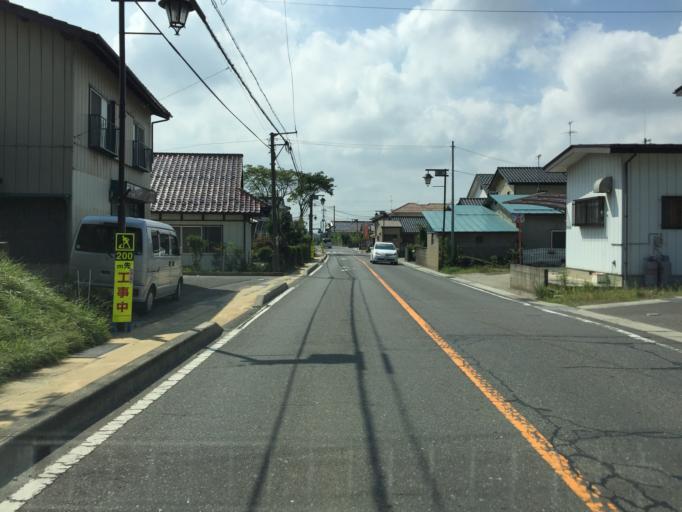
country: JP
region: Fukushima
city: Koriyama
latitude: 37.4517
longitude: 140.3906
